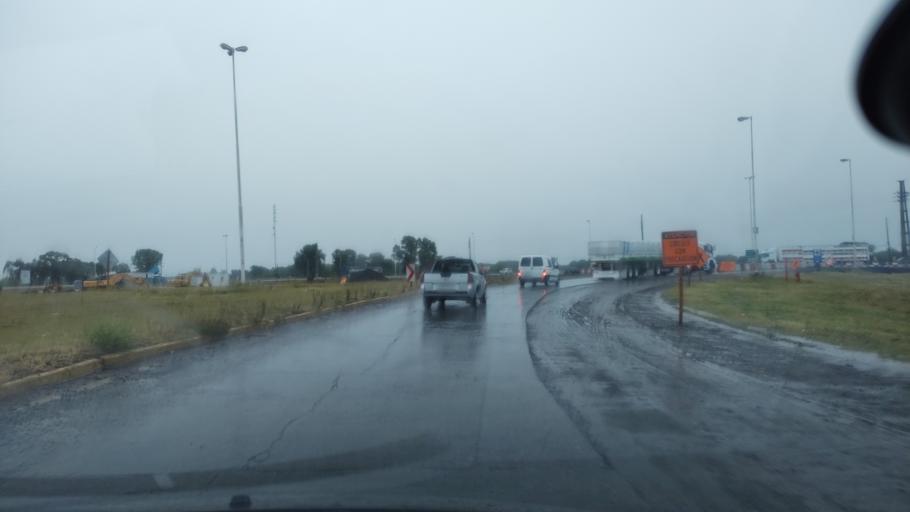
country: AR
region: Buenos Aires
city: Canuelas
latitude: -35.0210
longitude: -58.7472
